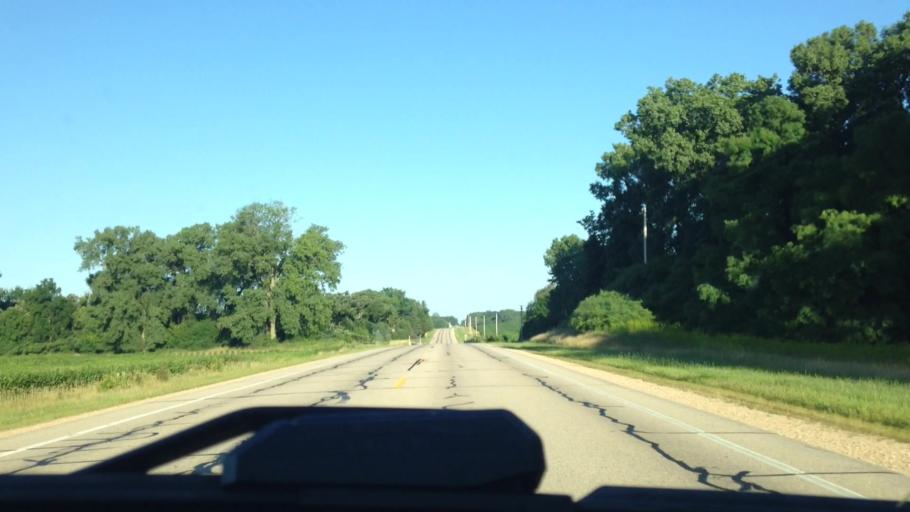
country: US
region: Wisconsin
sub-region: Columbia County
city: Fall River
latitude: 43.3407
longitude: -89.1244
